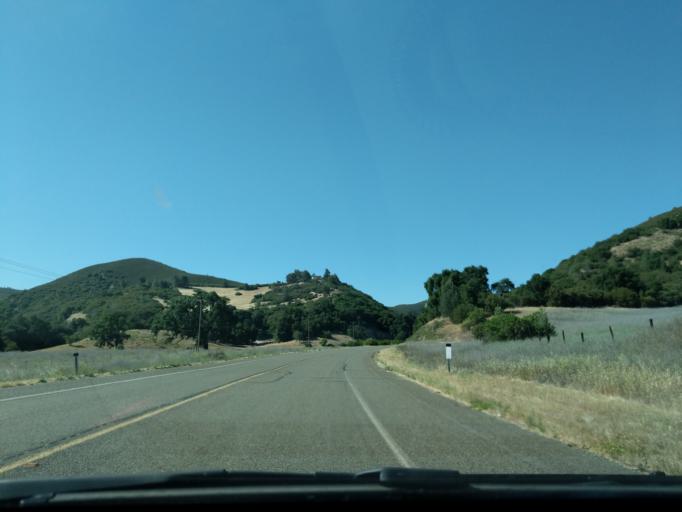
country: US
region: California
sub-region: Monterey County
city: King City
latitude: 36.0614
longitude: -121.1847
